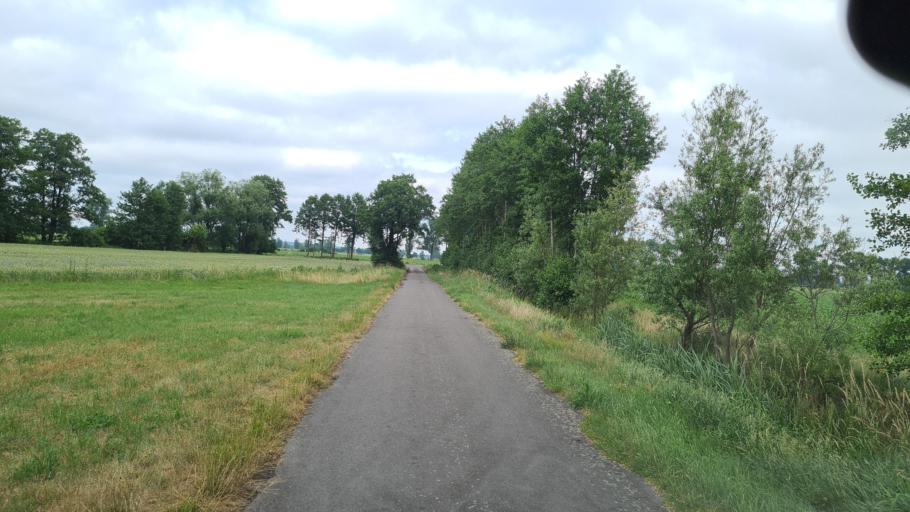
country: DE
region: Brandenburg
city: Groden
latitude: 51.4099
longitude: 13.5803
